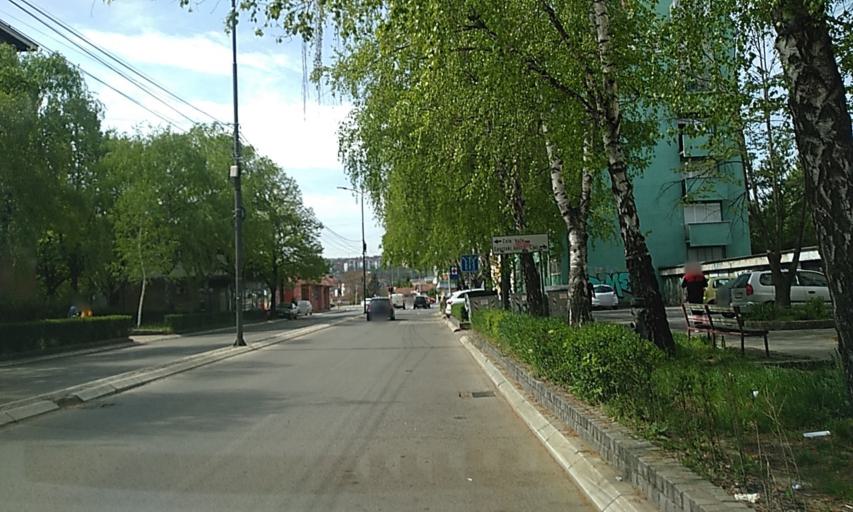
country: RS
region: Central Serbia
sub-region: Nisavski Okrug
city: Nis
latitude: 43.3163
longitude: 21.9174
